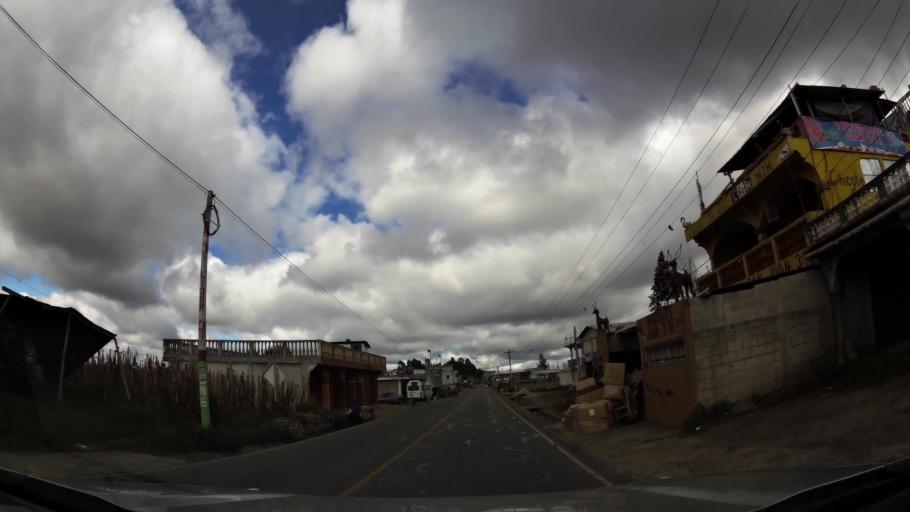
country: GT
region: Quiche
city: Chichicastenango
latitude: 14.8756
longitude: -91.1374
